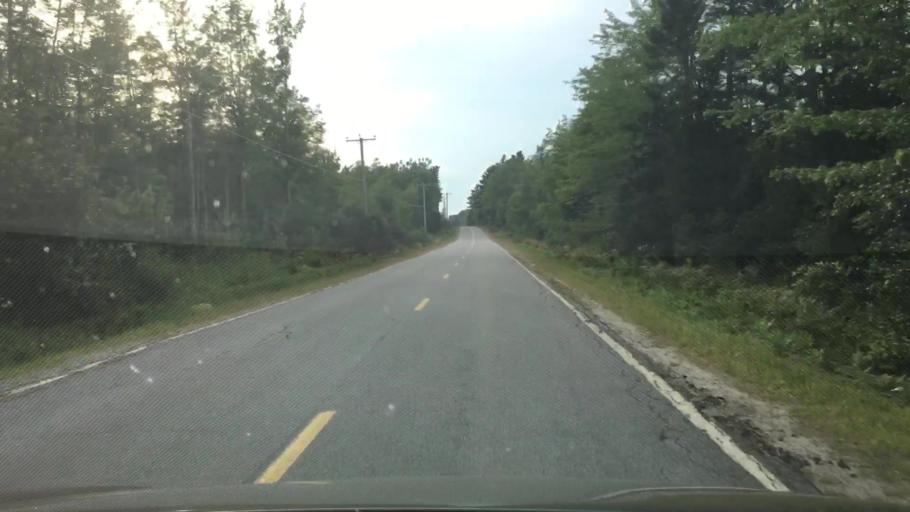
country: US
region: Maine
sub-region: Hancock County
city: Penobscot
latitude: 44.4713
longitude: -68.7515
